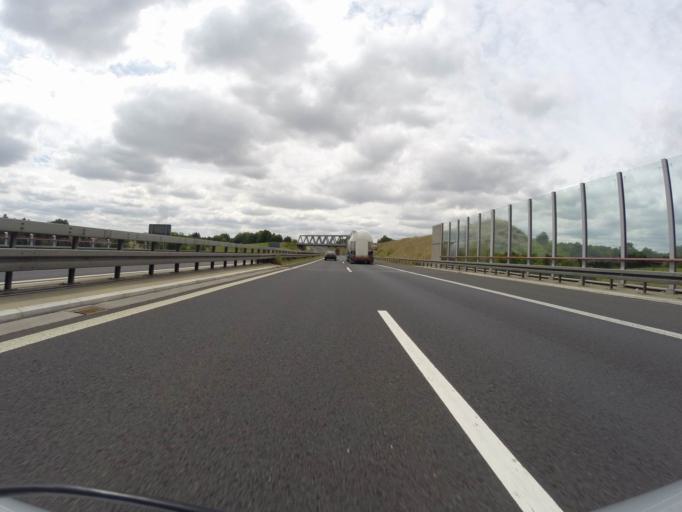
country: DE
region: Bavaria
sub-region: Regierungsbezirk Unterfranken
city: Poppenhausen
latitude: 50.0808
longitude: 10.1496
